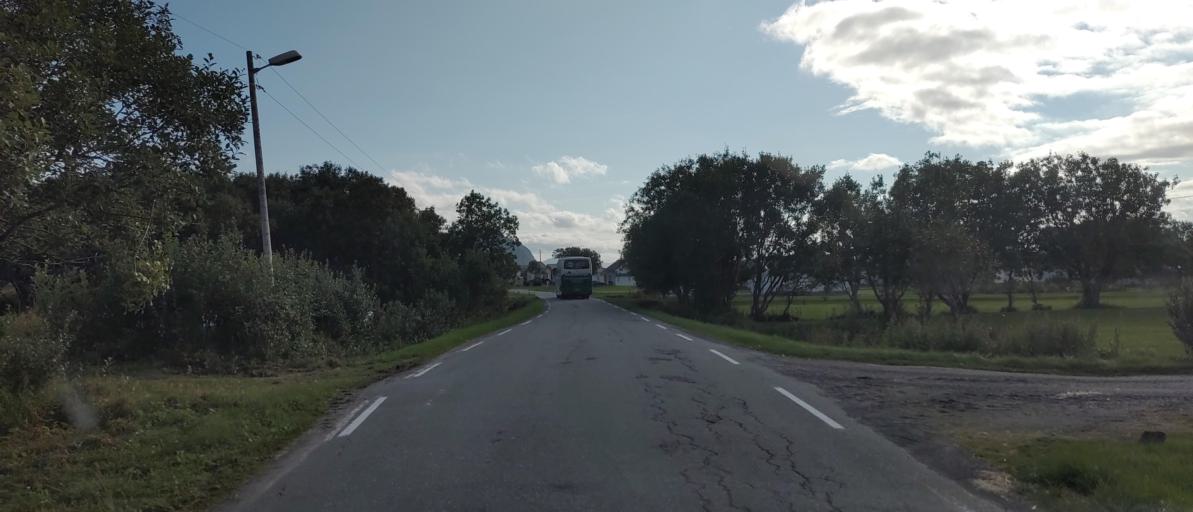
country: NO
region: Nordland
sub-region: Sortland
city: Sortland
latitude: 69.0467
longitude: 15.5164
